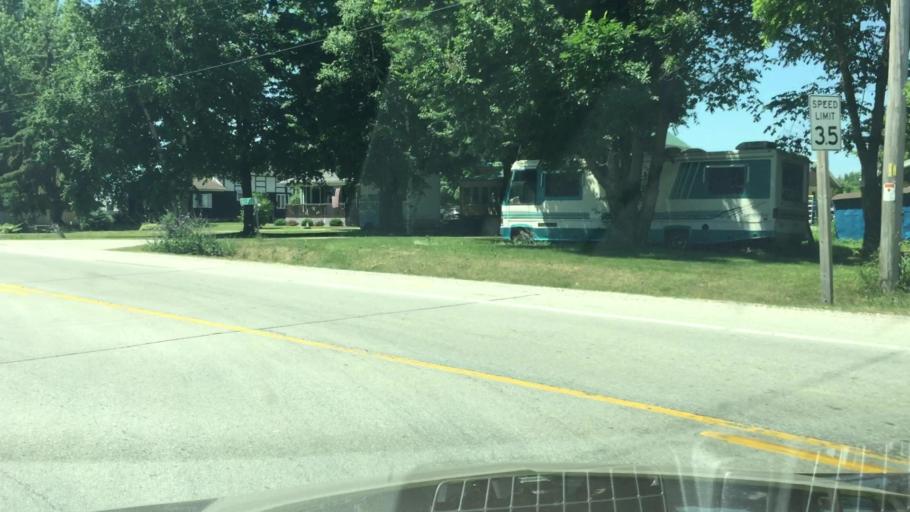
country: US
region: Wisconsin
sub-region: Fond du Lac County
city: Saint Peter
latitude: 43.9696
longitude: -88.3083
